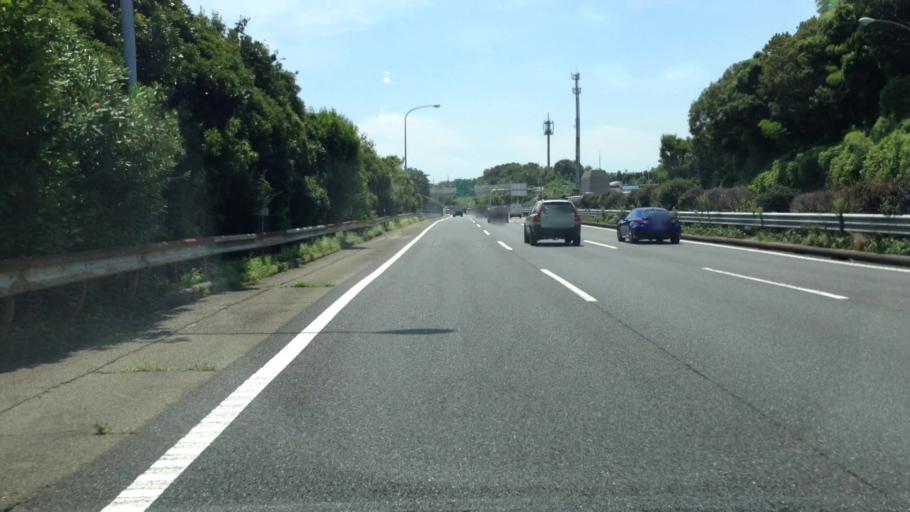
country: JP
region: Kanagawa
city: Yokohama
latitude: 35.5028
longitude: 139.5924
